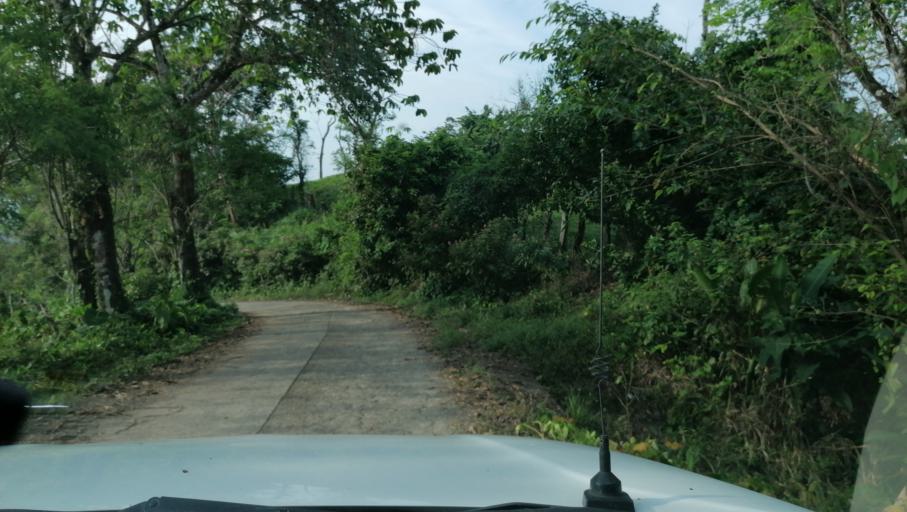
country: MX
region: Chiapas
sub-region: Juarez
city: El Triunfo 1ra. Seccion (Cardona)
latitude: 17.4851
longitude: -93.2362
